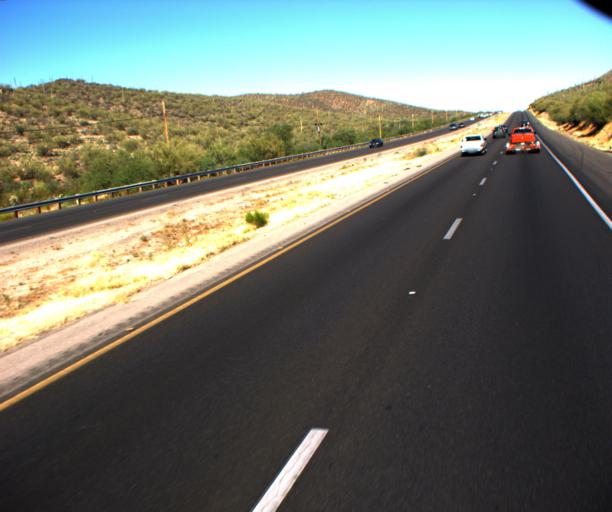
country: US
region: Arizona
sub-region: Pima County
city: Drexel Heights
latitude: 32.1770
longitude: -111.0317
